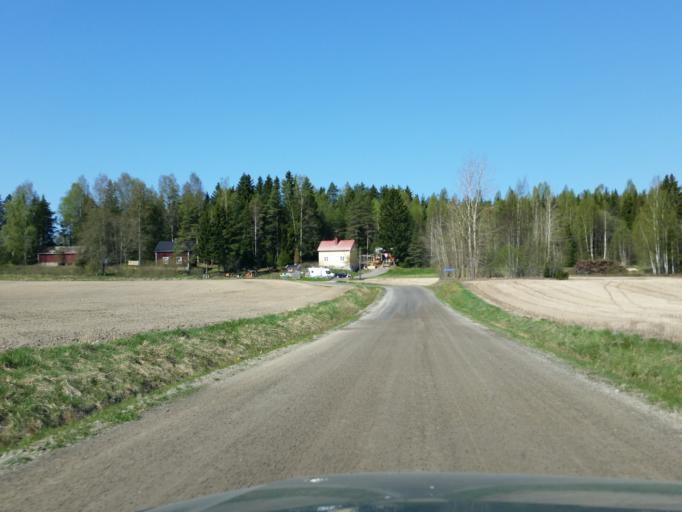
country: FI
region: Uusimaa
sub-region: Raaseporin
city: Karis
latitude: 60.1376
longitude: 23.6962
